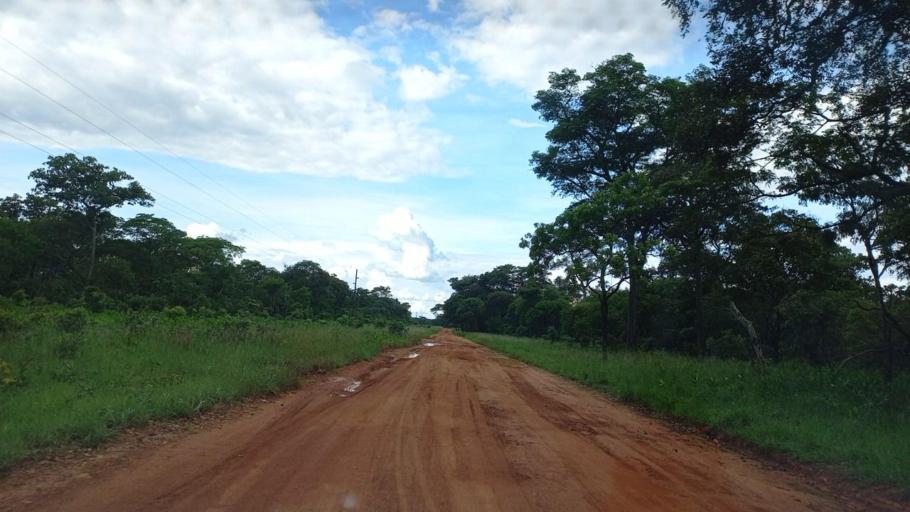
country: ZM
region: North-Western
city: Mwinilunga
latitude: -11.7967
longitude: 24.3712
